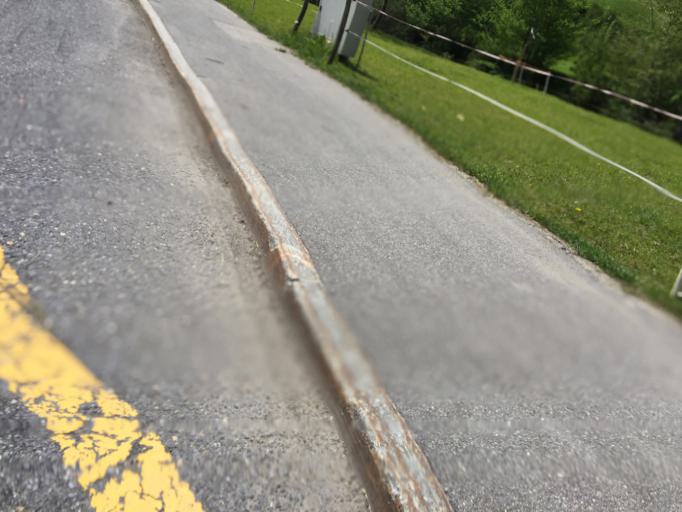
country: CH
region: Lucerne
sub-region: Entlebuch District
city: Escholzmatt
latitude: 46.8955
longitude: 7.9088
